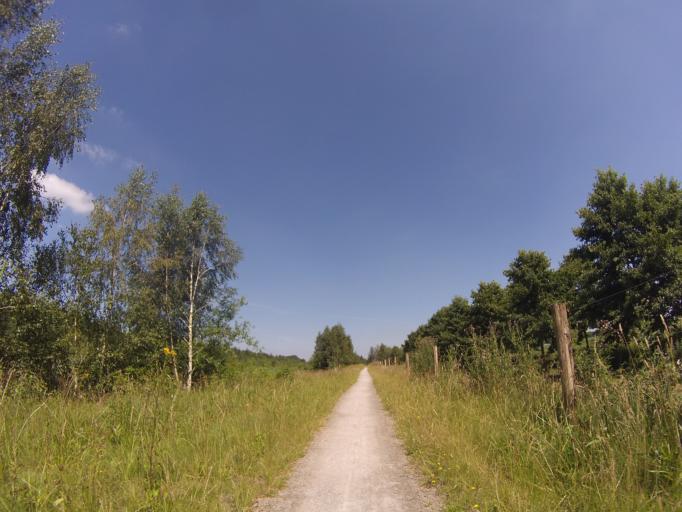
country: NL
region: Drenthe
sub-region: Gemeente Emmen
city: Klazienaveen
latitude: 52.7486
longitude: 7.0257
